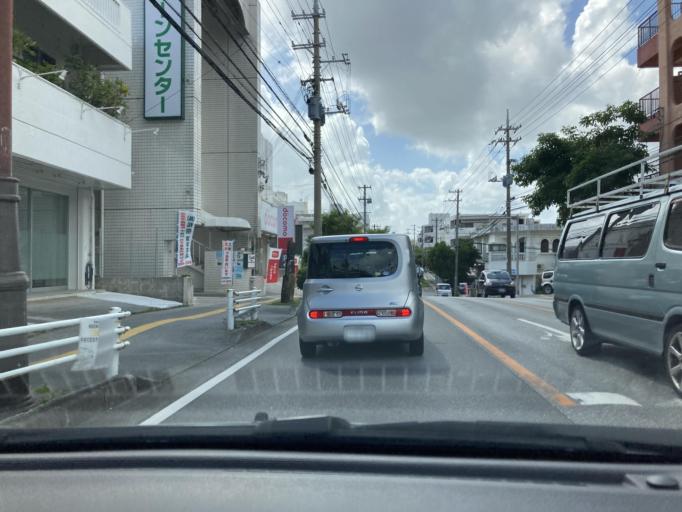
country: JP
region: Okinawa
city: Ginowan
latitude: 26.2543
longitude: 127.7198
